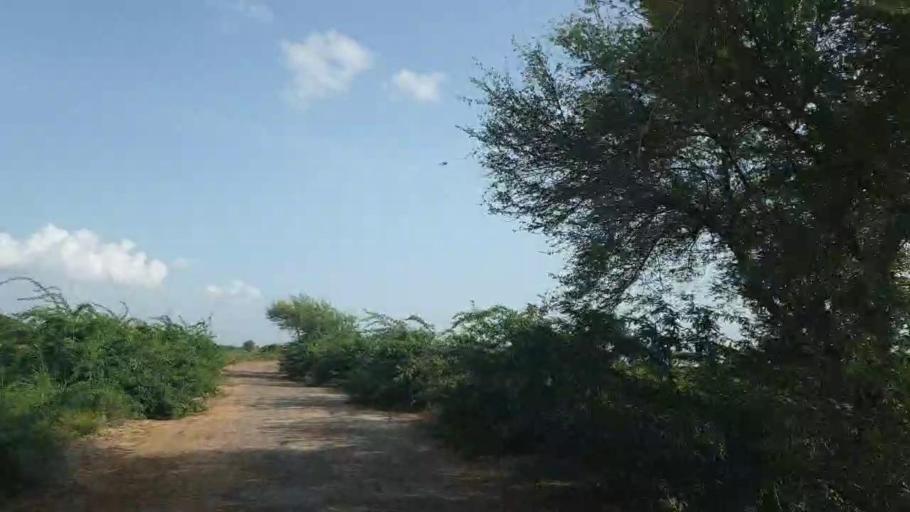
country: PK
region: Sindh
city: Kadhan
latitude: 24.6181
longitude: 69.0958
